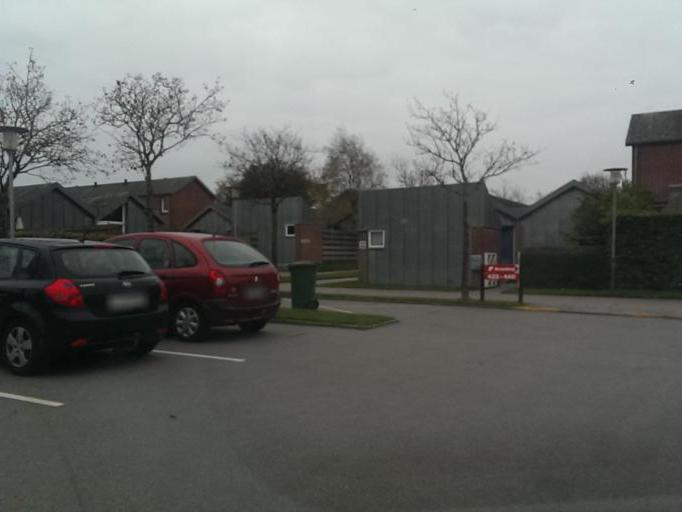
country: DK
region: South Denmark
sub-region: Esbjerg Kommune
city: Esbjerg
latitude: 55.5177
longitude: 8.4369
